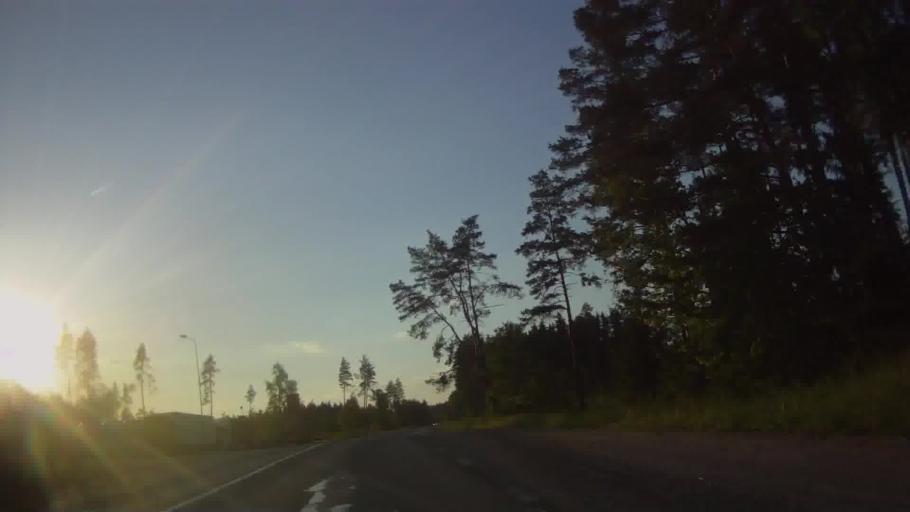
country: LV
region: Jekabpils Rajons
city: Jekabpils
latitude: 56.5342
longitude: 25.8196
